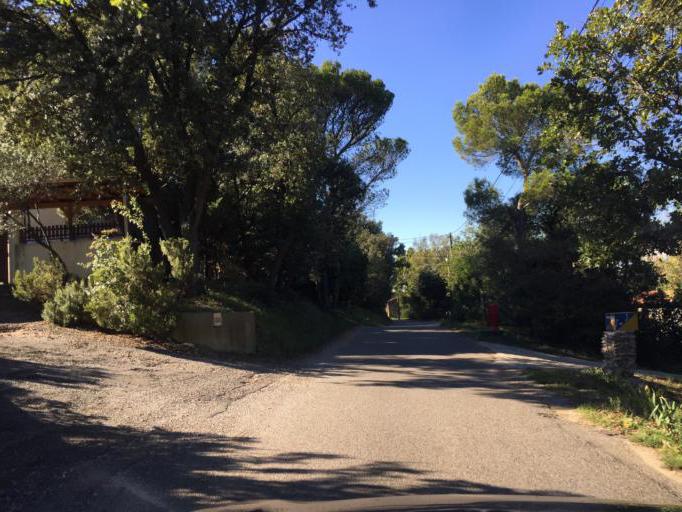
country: FR
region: Provence-Alpes-Cote d'Azur
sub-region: Departement du Vaucluse
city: Piolenc
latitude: 44.1748
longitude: 4.7769
